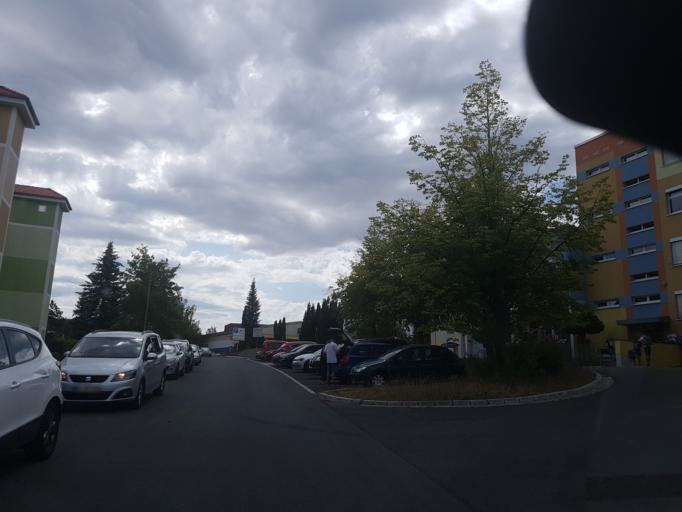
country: DE
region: Saxony
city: Waldheim
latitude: 51.0740
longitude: 13.0100
